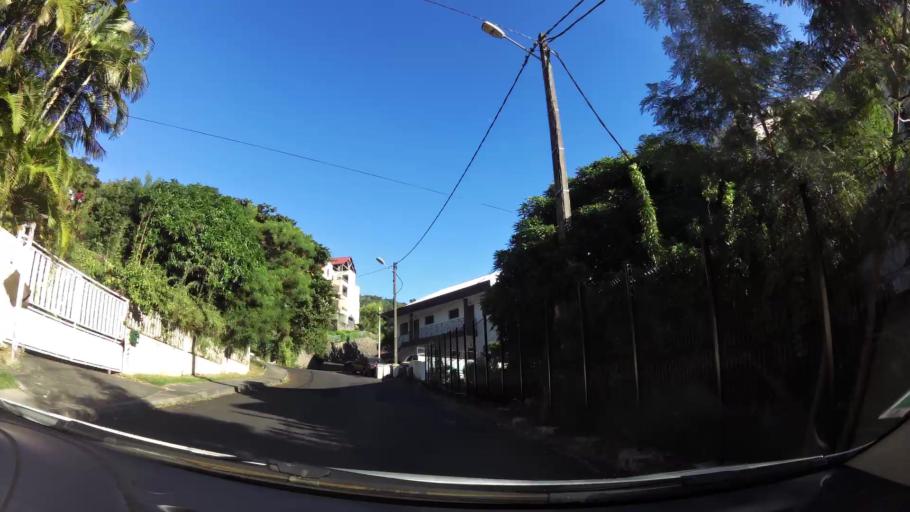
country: RE
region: Reunion
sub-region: Reunion
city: Saint-Denis
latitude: -20.8926
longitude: 55.4477
